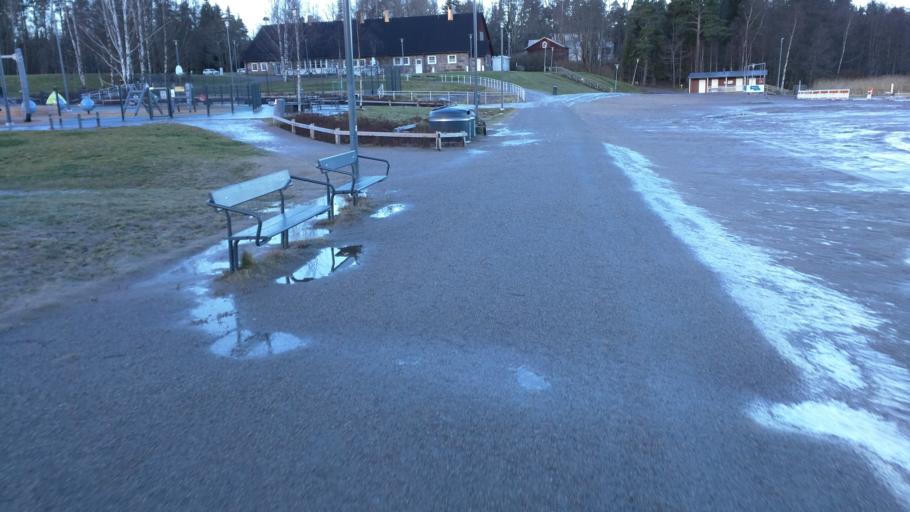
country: FI
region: Uusimaa
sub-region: Helsinki
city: Espoo
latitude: 60.2408
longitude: 24.6599
